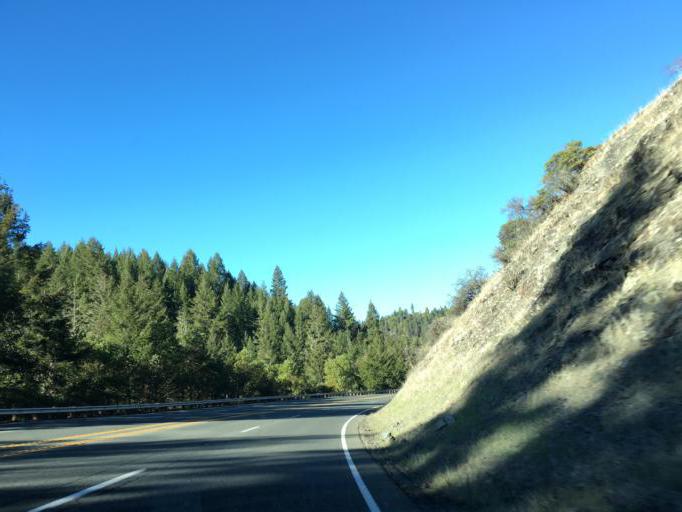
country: US
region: California
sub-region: Mendocino County
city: Laytonville
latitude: 39.6102
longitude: -123.4588
